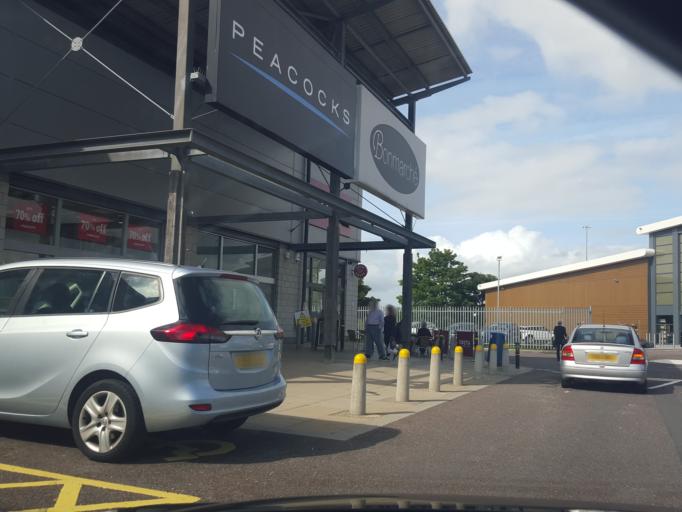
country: GB
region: England
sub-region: Suffolk
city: Shotley Gate
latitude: 51.9409
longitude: 1.2584
